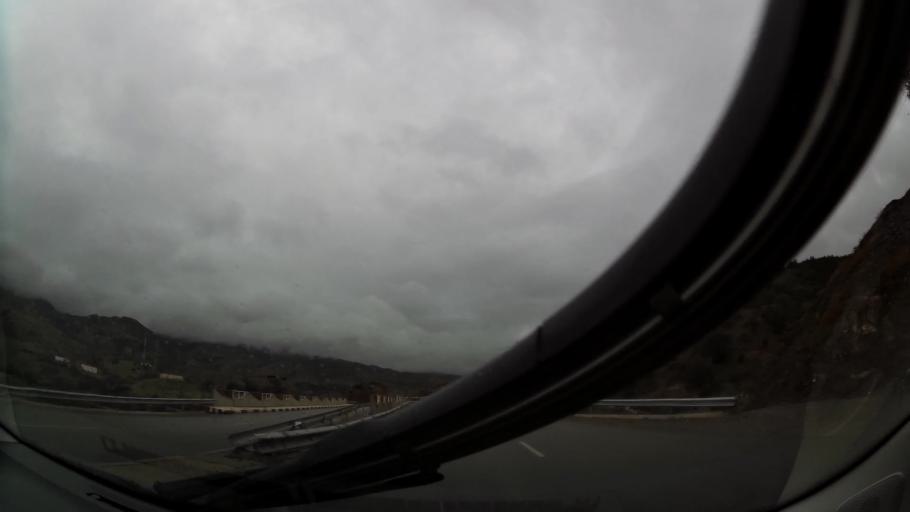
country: MA
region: Taza-Al Hoceima-Taounate
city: Imzourene
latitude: 34.9928
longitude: -3.8117
